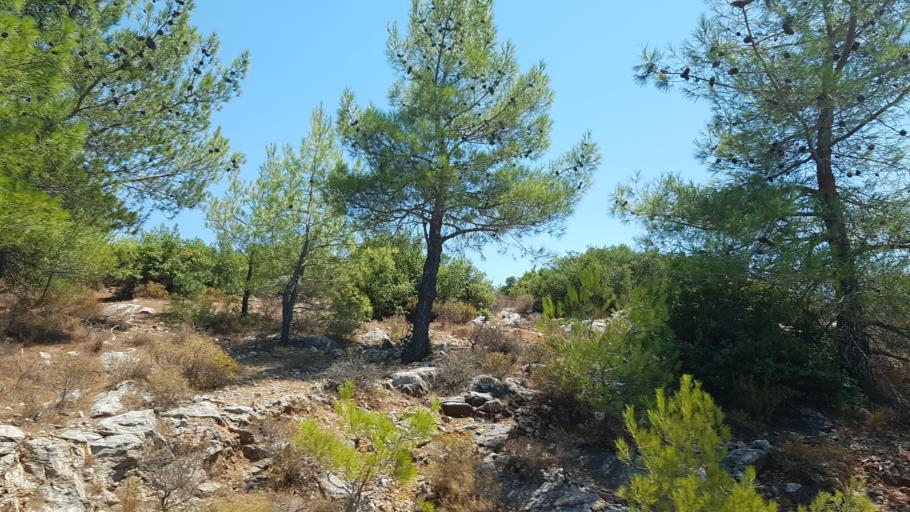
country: TR
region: Mugla
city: Karaova
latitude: 37.0164
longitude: 27.7263
